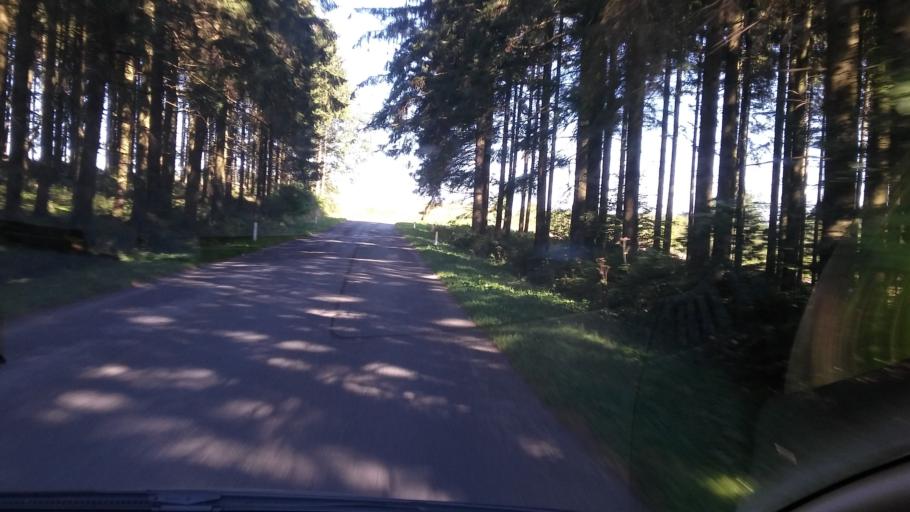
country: BE
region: Wallonia
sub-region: Province du Luxembourg
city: Neufchateau
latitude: 49.8109
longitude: 5.4140
